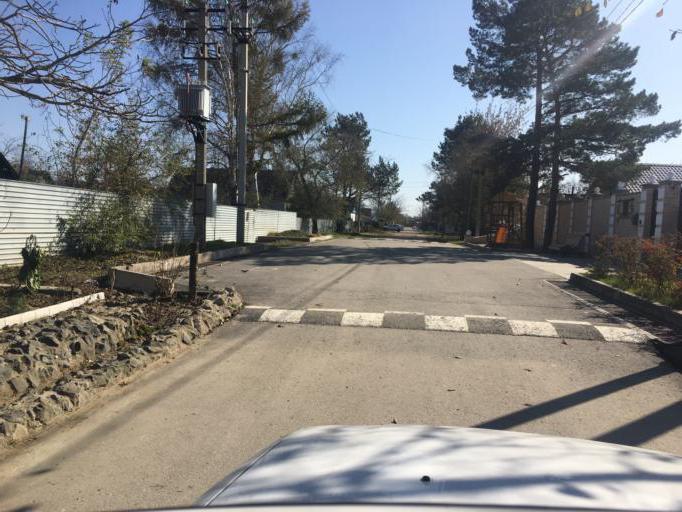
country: RU
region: Primorskiy
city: Dal'nerechensk
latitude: 45.9295
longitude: 133.7482
